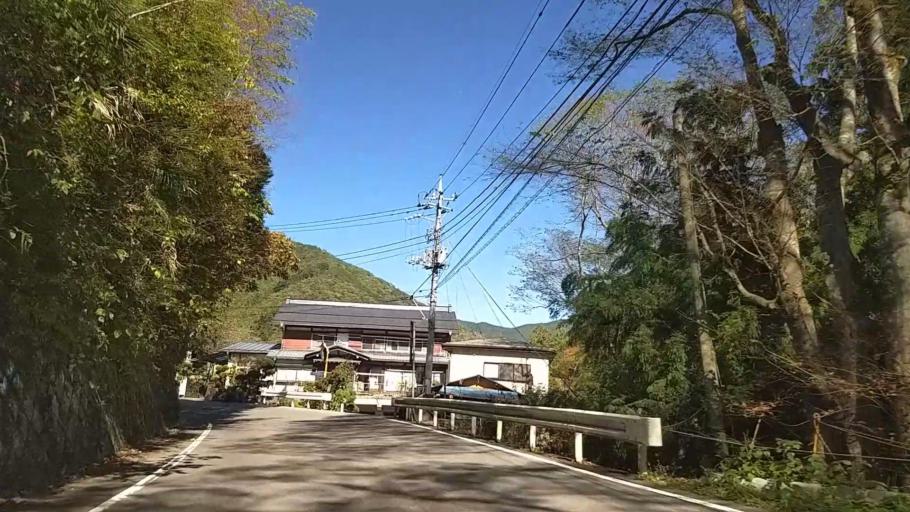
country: JP
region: Yamanashi
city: Uenohara
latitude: 35.6508
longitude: 139.0980
